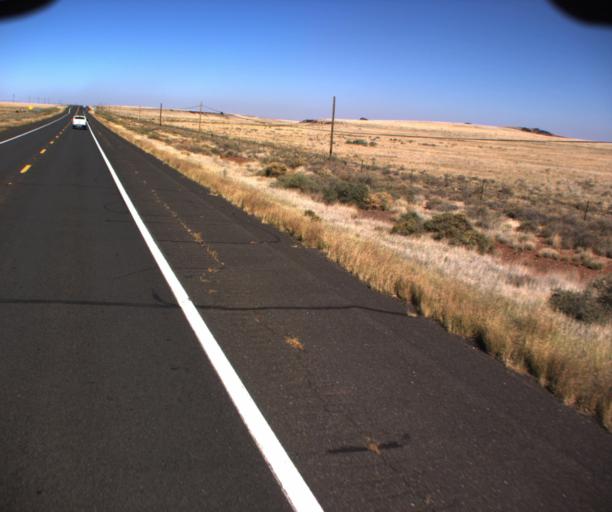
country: US
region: Arizona
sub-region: Coconino County
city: Flagstaff
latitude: 35.6408
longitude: -111.5181
